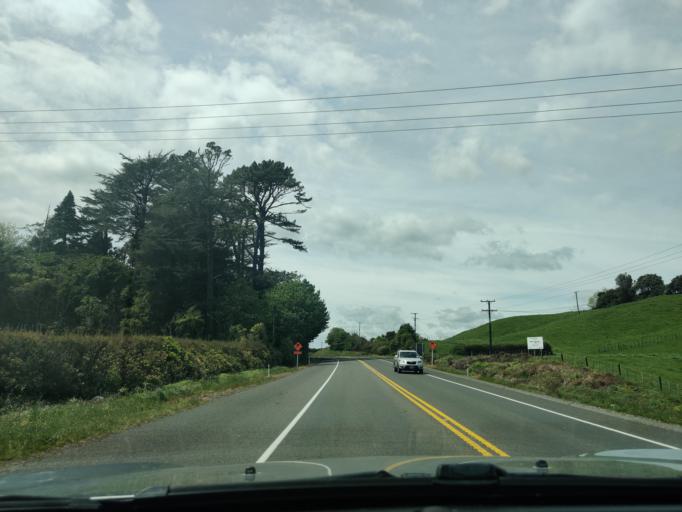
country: NZ
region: Taranaki
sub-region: New Plymouth District
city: New Plymouth
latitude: -39.1507
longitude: 174.1547
